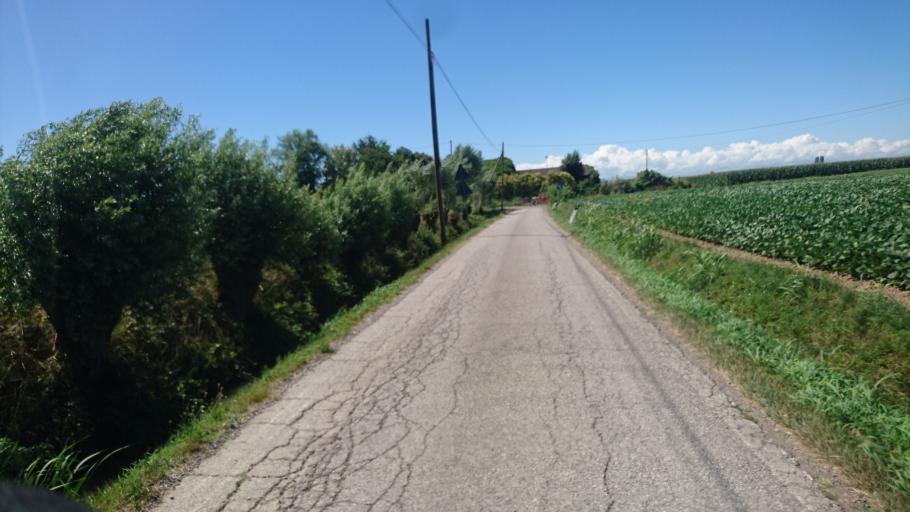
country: IT
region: Veneto
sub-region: Provincia di Padova
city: Pontelongo
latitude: 45.2627
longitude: 12.0145
